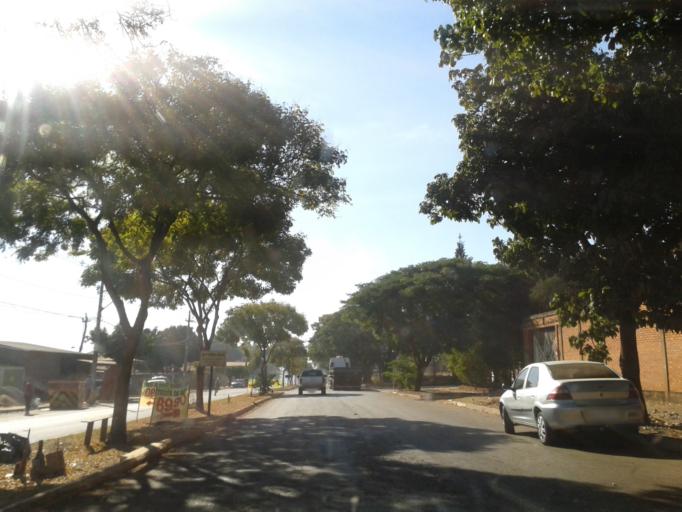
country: BR
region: Goias
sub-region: Goiania
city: Goiania
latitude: -16.6525
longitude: -49.3381
